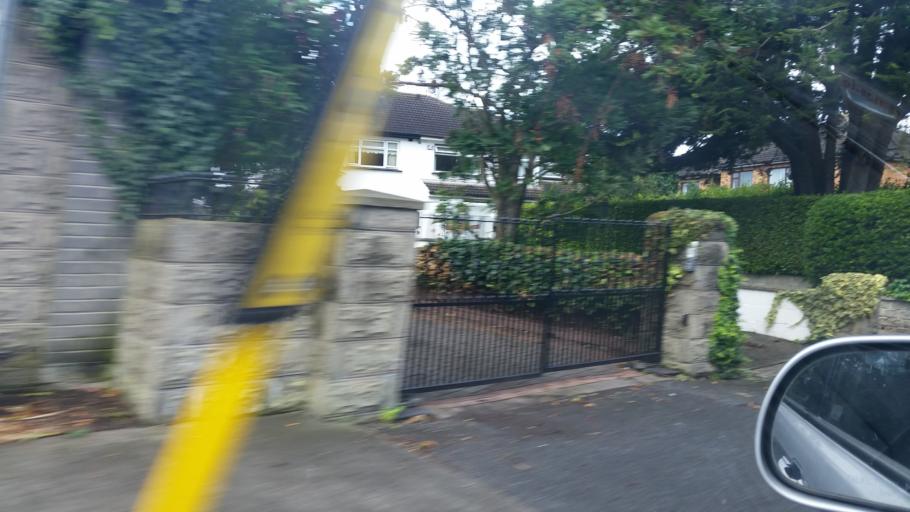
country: IE
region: Leinster
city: Portmarnock
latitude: 53.4312
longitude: -6.1347
